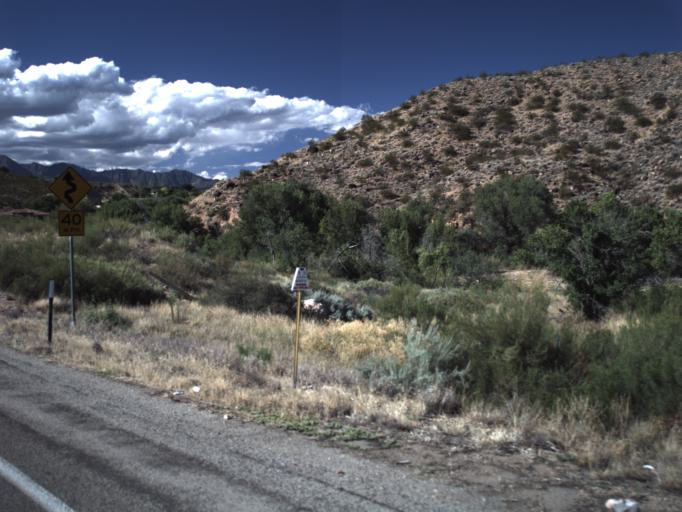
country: US
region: Utah
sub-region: Washington County
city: LaVerkin
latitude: 37.2220
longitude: -113.2786
